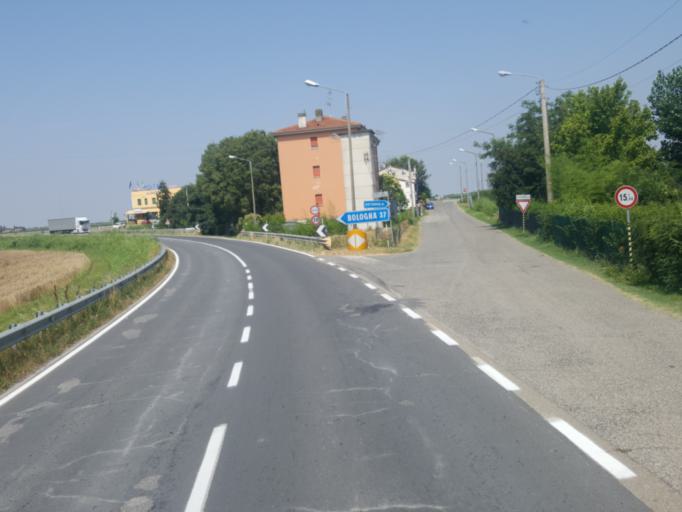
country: IT
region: Emilia-Romagna
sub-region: Provincia di Bologna
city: Sesto Imolese
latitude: 44.4685
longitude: 11.7707
